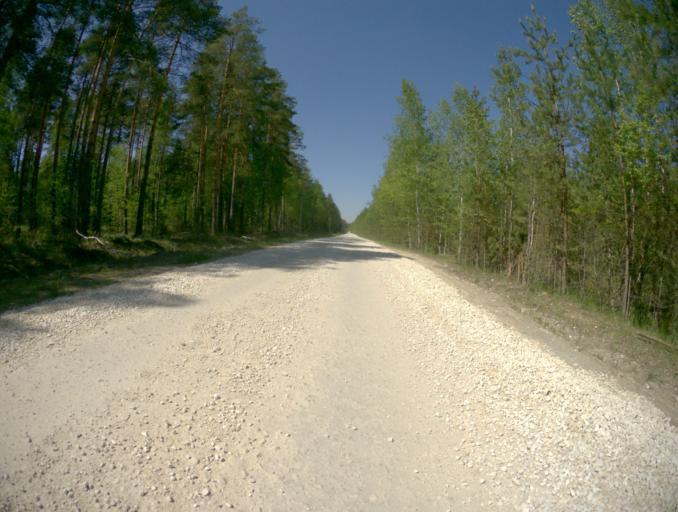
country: RU
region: Vladimir
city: Gusevskiy
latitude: 55.7205
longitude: 40.5904
